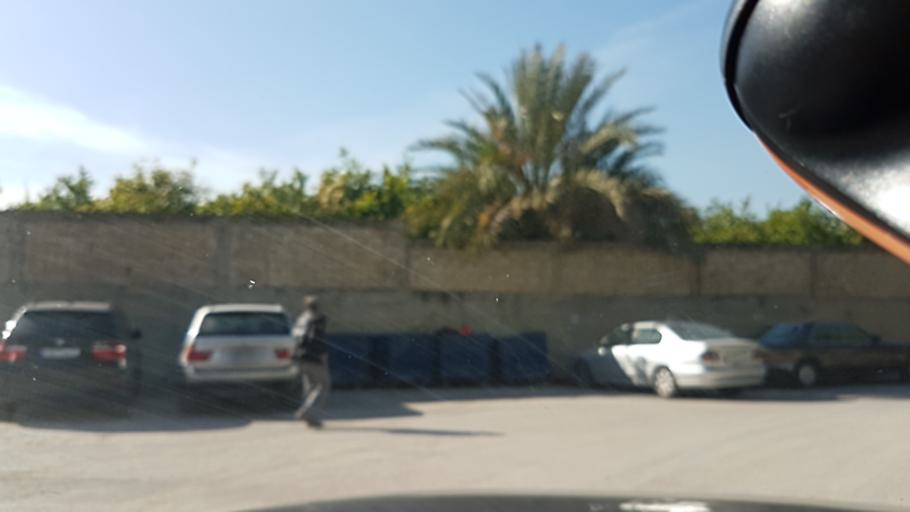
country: LB
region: Liban-Sud
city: Sidon
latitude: 33.5811
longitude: 35.3897
